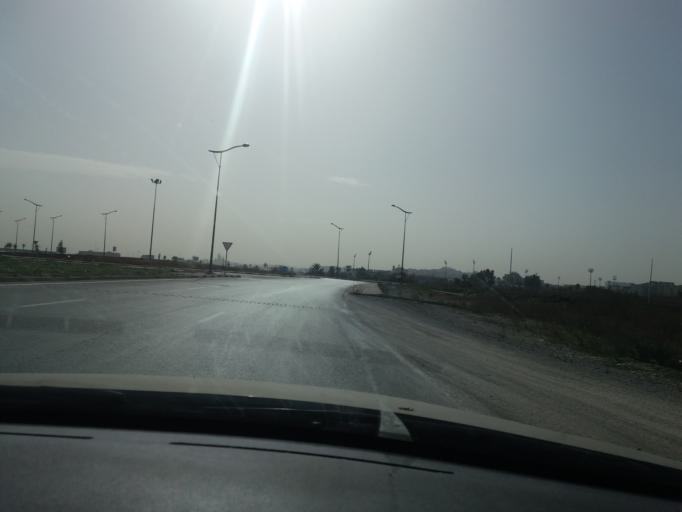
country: TN
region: Tunis
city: Tunis
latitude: 36.8082
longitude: 10.1934
